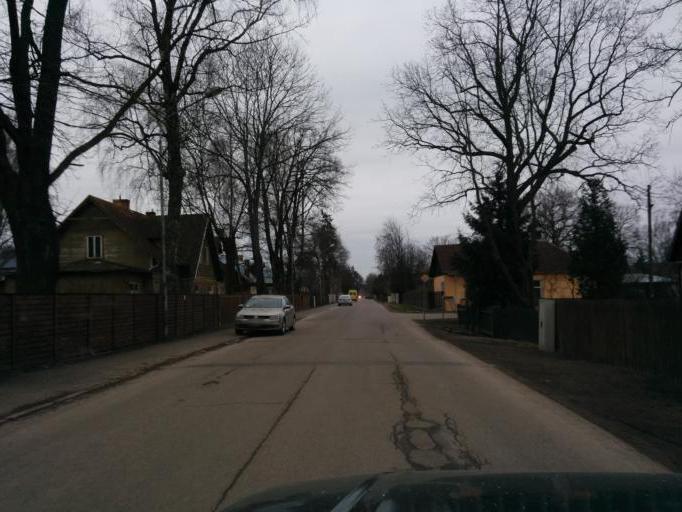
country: LV
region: Jurmala
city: Jurmala
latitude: 56.9660
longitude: 23.8178
